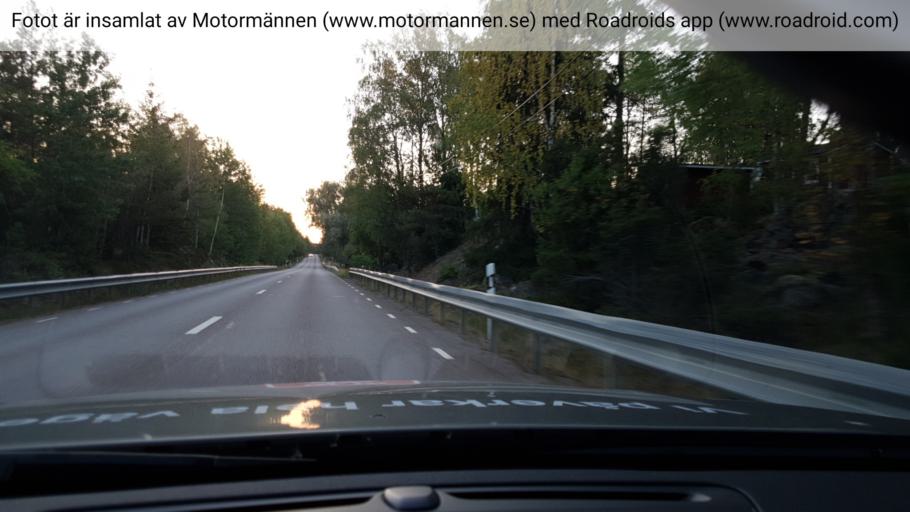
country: SE
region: Uppsala
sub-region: Osthammars Kommun
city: Bjorklinge
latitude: 59.9848
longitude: 17.3306
